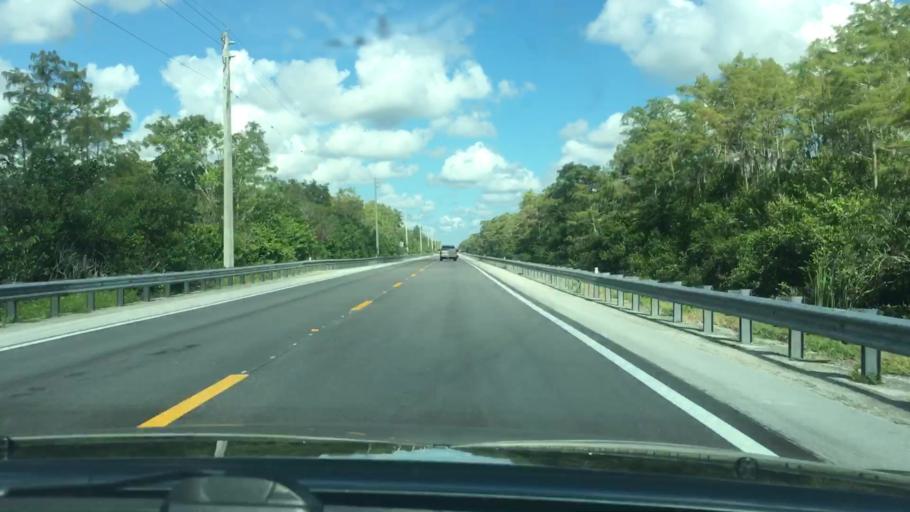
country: US
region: Florida
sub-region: Miami-Dade County
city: Kendall West
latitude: 25.7668
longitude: -80.8333
